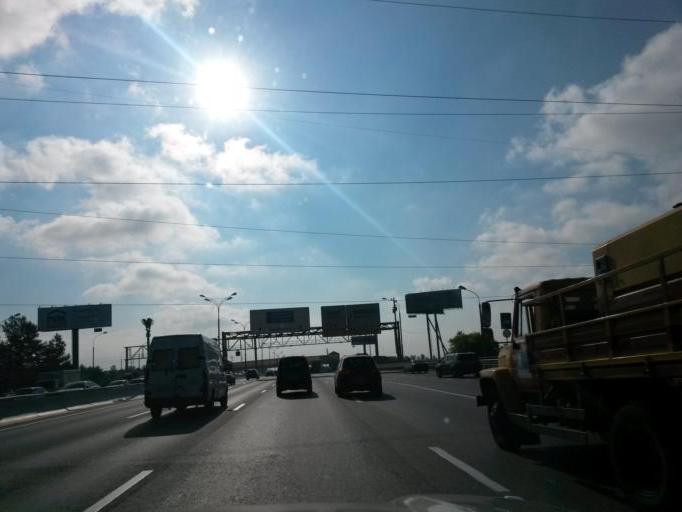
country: RU
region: Moskovskaya
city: Biryulevo Zapadnoye
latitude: 55.5732
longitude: 37.6434
